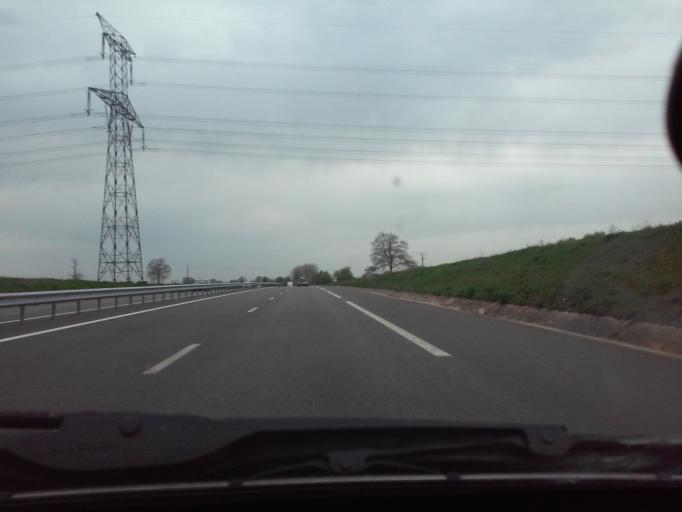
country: FR
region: Brittany
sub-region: Departement d'Ille-et-Vilaine
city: Romagne
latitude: 48.3548
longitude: -1.2470
